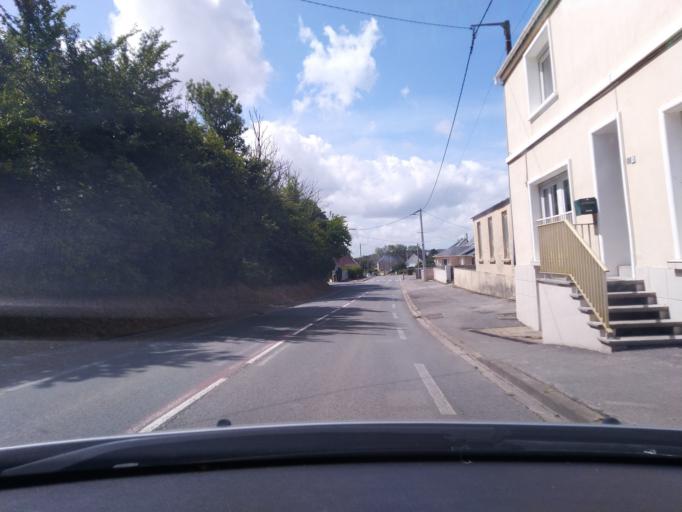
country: FR
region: Nord-Pas-de-Calais
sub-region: Departement du Pas-de-Calais
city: Ferques
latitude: 50.8348
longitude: 1.7605
